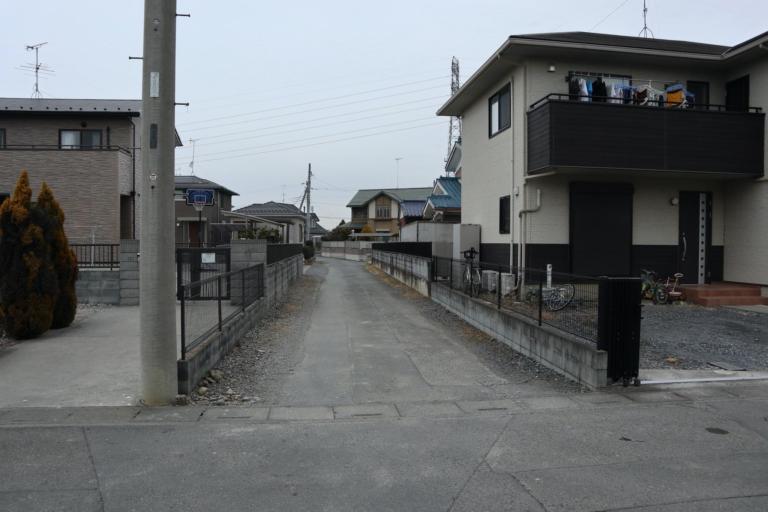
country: JP
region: Saitama
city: Gyoda
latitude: 36.1213
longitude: 139.4519
